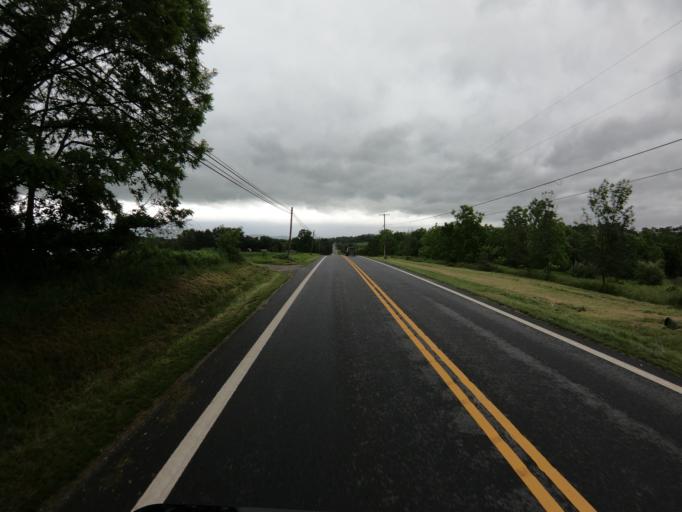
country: US
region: Maryland
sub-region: Frederick County
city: Myersville
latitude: 39.4710
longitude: -77.5997
